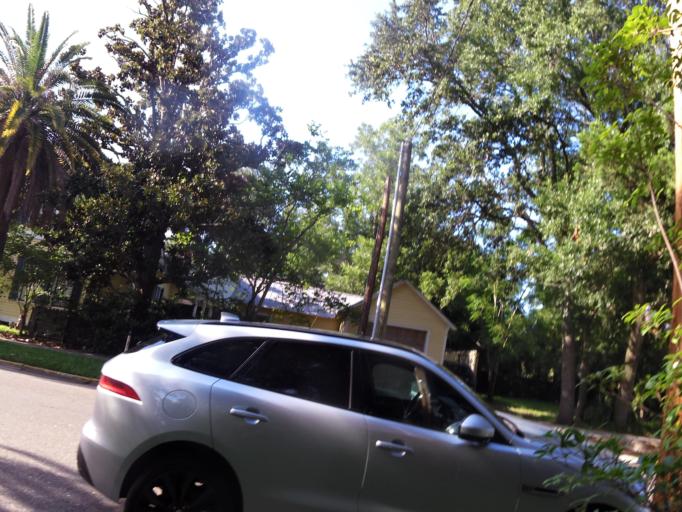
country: US
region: Florida
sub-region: Nassau County
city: Fernandina Beach
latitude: 30.6698
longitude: -81.4628
